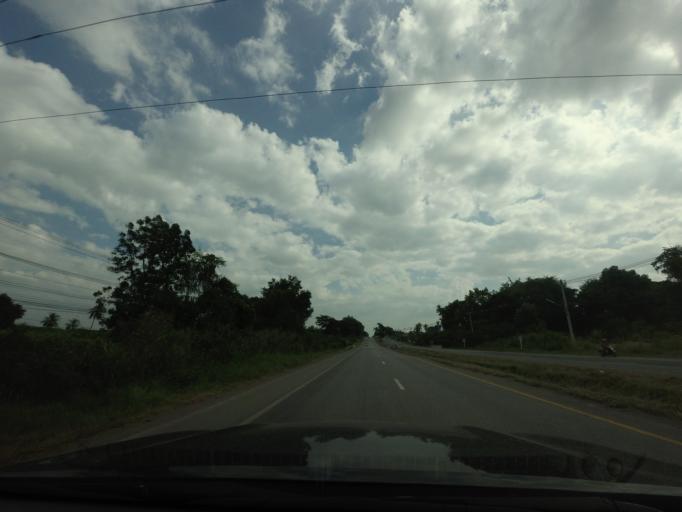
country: TH
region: Lop Buri
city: Chai Badan
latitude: 15.2779
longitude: 101.1239
